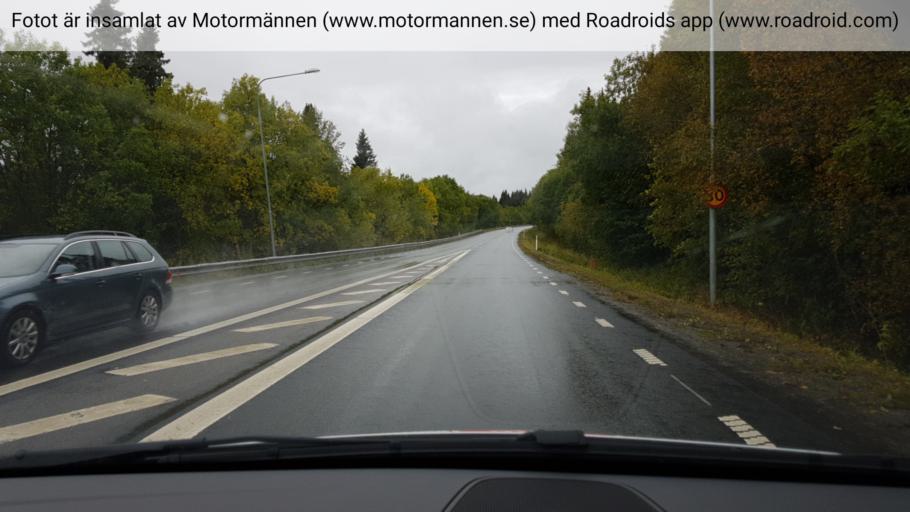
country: SE
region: Jaemtland
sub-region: Are Kommun
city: Are
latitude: 63.3987
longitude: 12.9718
